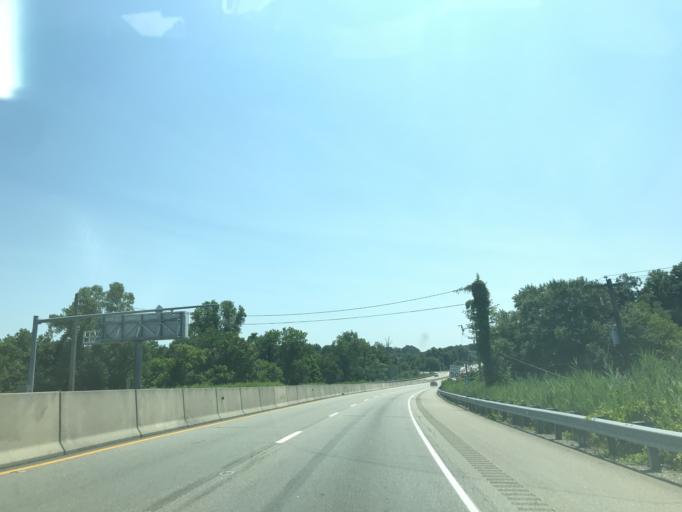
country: US
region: Pennsylvania
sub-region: Chester County
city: West Chester
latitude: 39.9493
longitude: -75.5825
